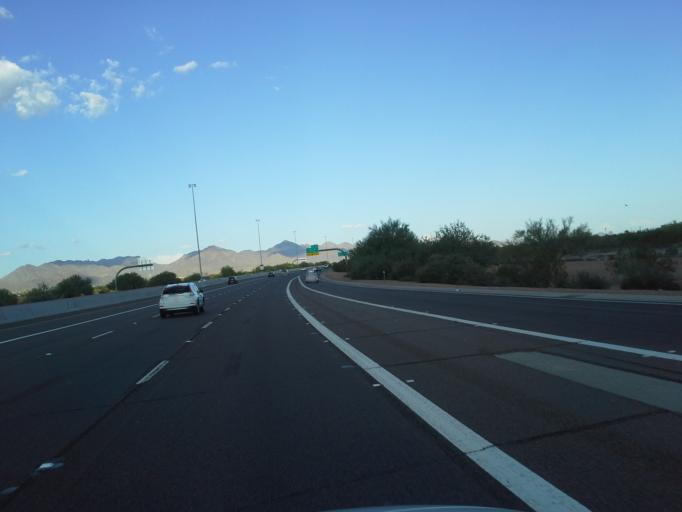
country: US
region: Arizona
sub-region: Maricopa County
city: Paradise Valley
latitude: 33.6727
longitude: -111.9731
